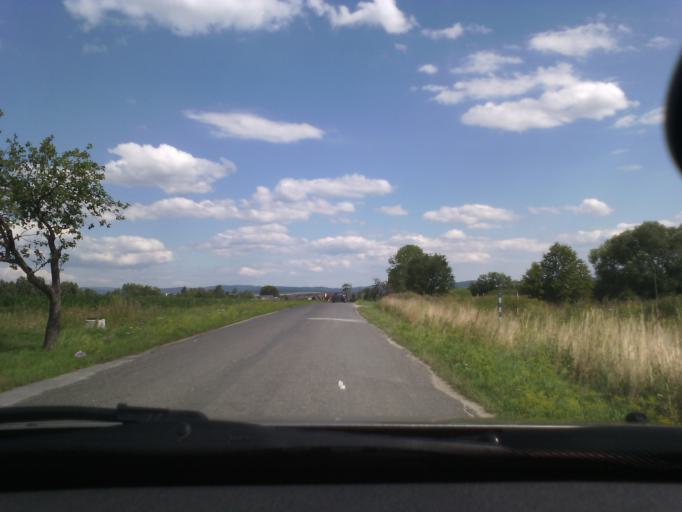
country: SK
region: Presovsky
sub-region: Okres Poprad
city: Poprad
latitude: 49.1219
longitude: 20.3439
